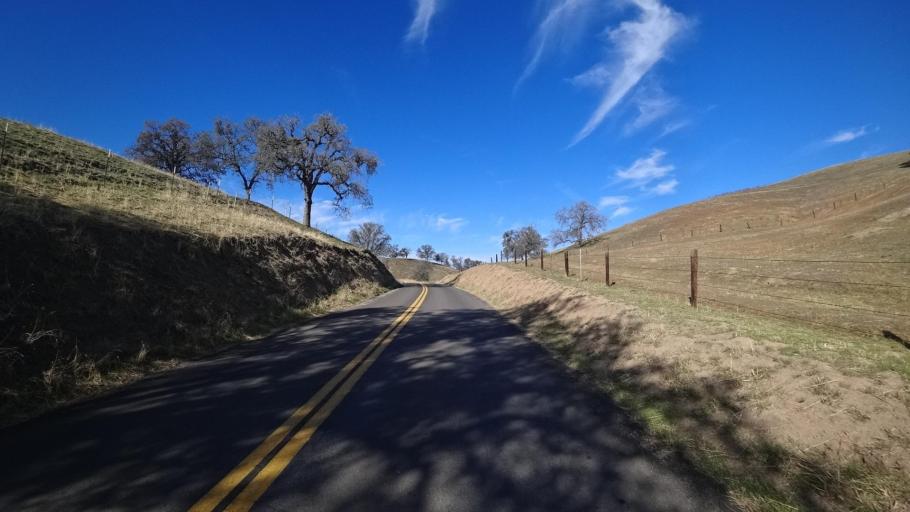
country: US
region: California
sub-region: Kern County
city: Oildale
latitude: 35.6590
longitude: -118.8430
